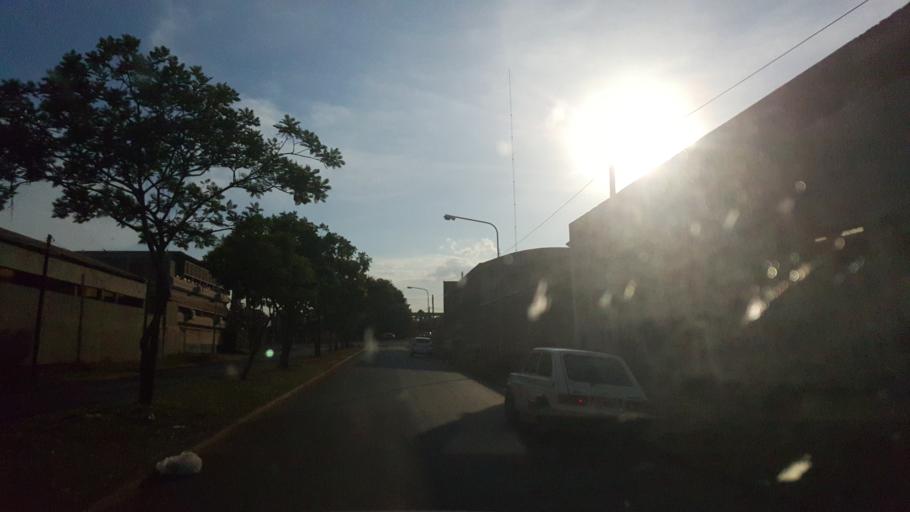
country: AR
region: Misiones
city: Garupa
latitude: -27.4371
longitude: -55.8814
